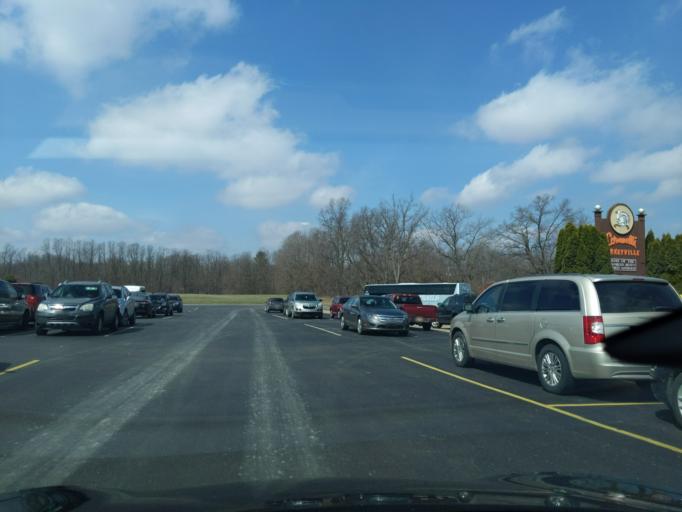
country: US
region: Michigan
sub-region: Calhoun County
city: Marshall
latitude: 42.3480
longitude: -84.9962
